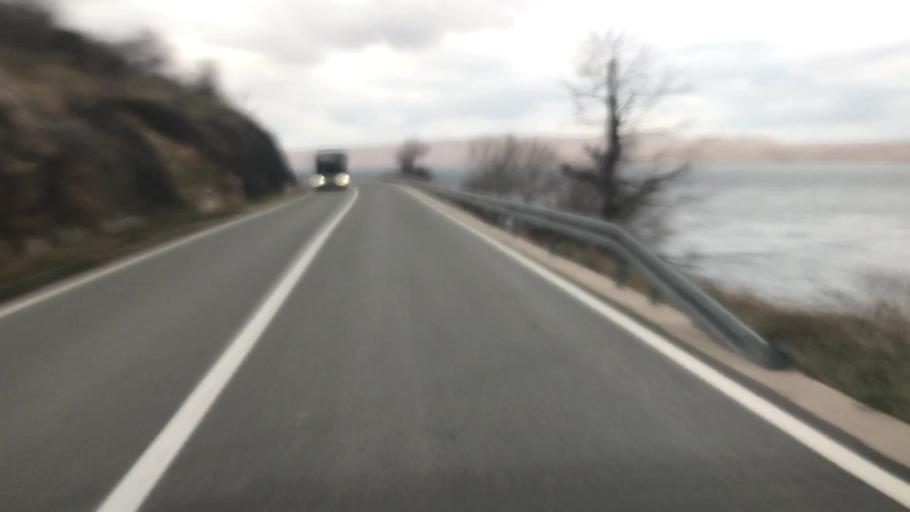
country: HR
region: Licko-Senjska
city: Karlobag
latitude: 44.5171
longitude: 15.0928
